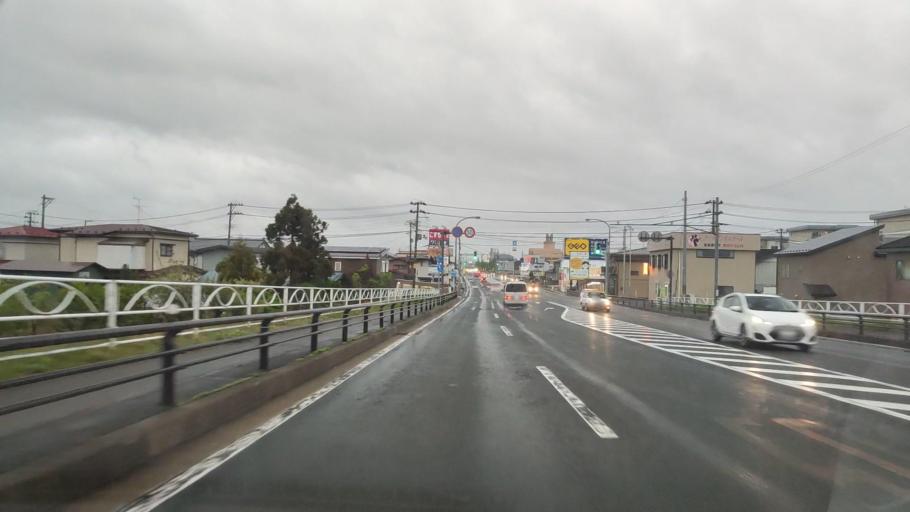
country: JP
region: Akita
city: Akita
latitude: 39.6958
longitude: 140.1194
